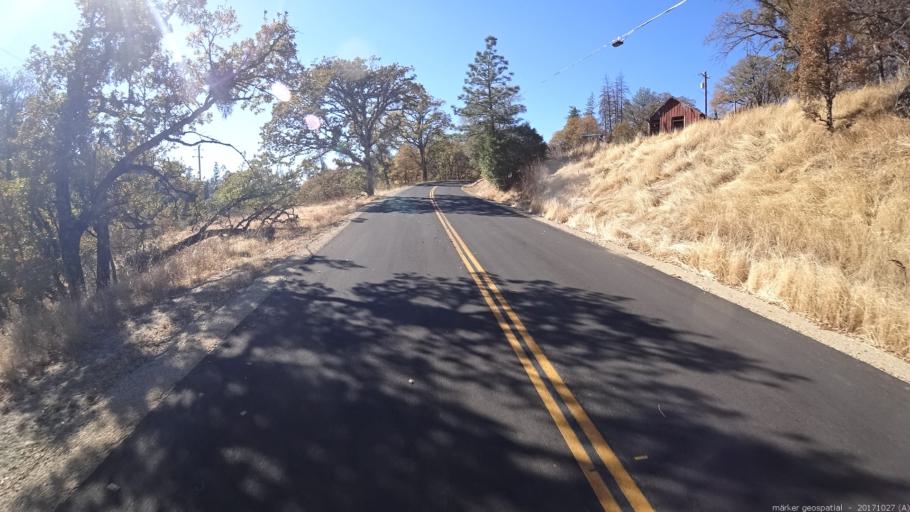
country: US
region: California
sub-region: Shasta County
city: Shingletown
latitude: 40.6793
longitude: -121.8724
